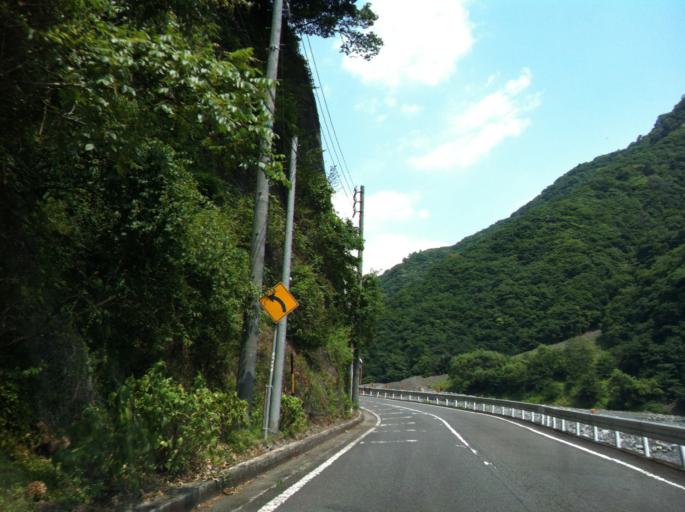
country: JP
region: Shizuoka
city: Shizuoka-shi
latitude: 35.2121
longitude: 138.3518
